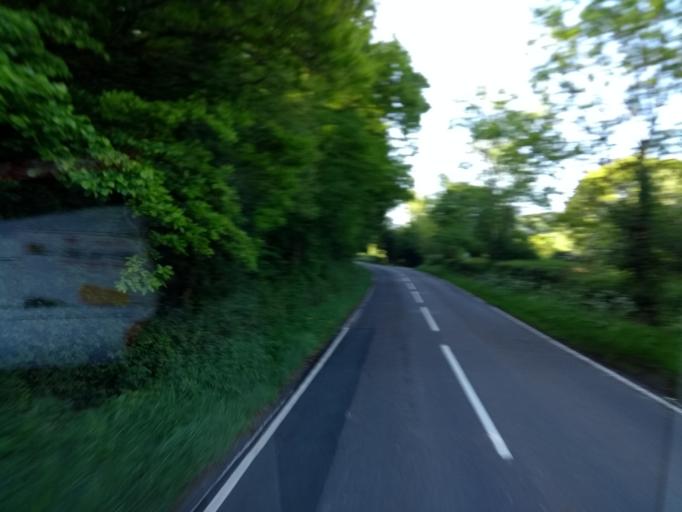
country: GB
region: England
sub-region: Somerset
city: Taunton
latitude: 50.9640
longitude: -3.0926
